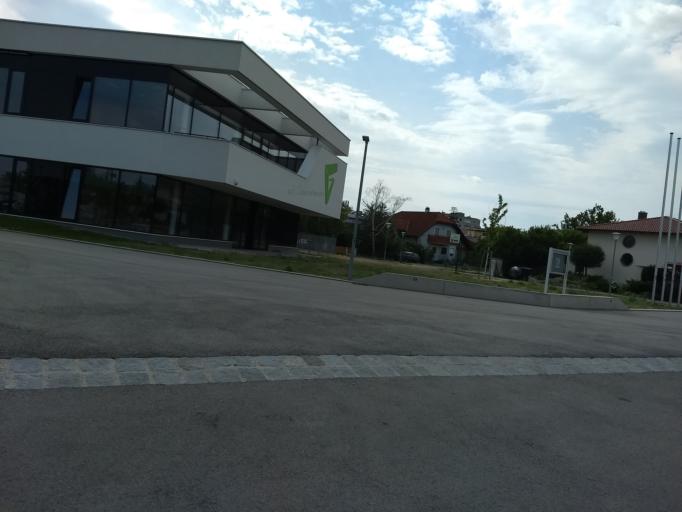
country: AT
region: Lower Austria
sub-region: Politischer Bezirk Modling
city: Guntramsdorf
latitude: 48.0516
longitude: 16.3149
